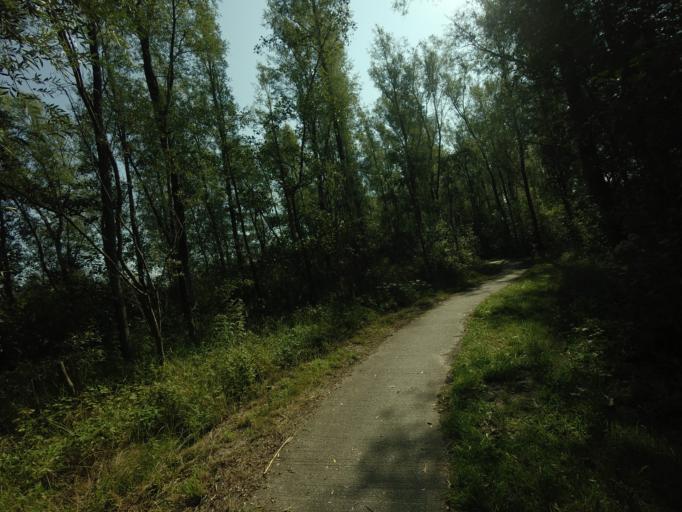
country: NL
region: Groningen
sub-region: Gemeente De Marne
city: Ulrum
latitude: 53.3917
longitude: 6.2572
